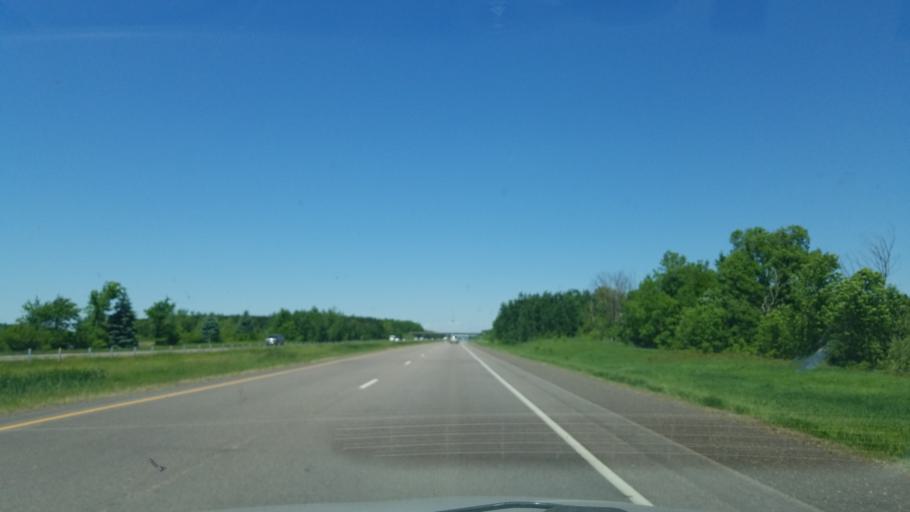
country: US
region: Minnesota
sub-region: Chisago County
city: Rush City
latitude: 45.7110
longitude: -92.9921
